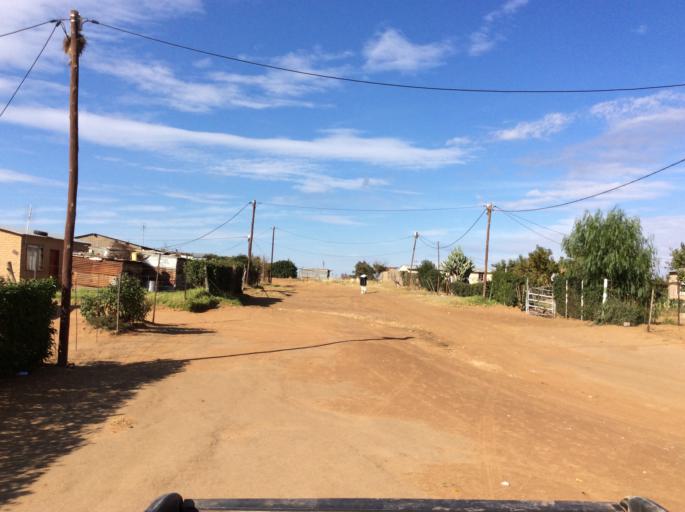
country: LS
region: Mafeteng
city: Mafeteng
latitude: -29.7158
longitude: 27.0126
